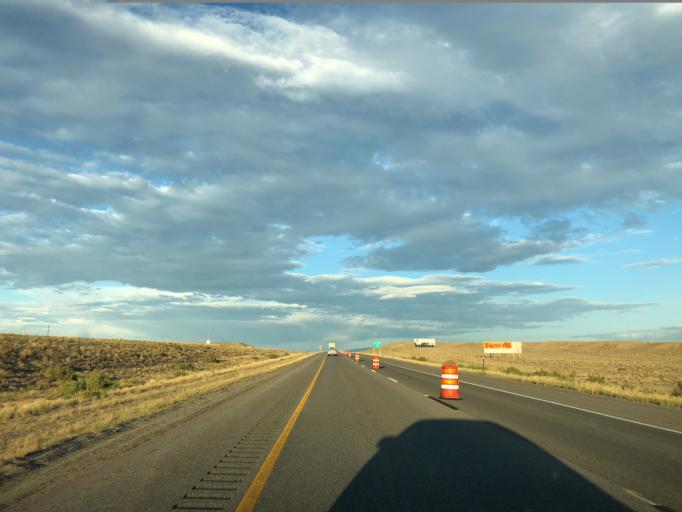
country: US
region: Wyoming
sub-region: Carbon County
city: Rawlins
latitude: 41.7579
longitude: -106.9836
